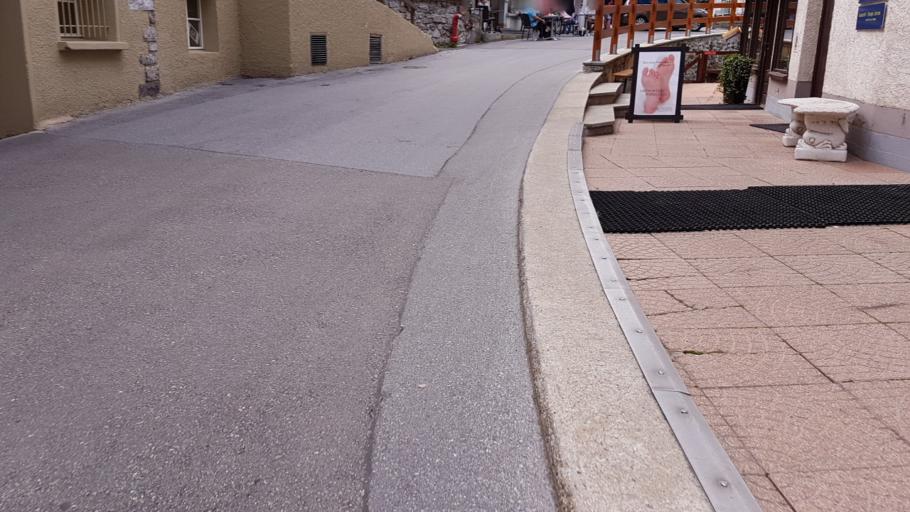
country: CH
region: Valais
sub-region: Leuk District
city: Leukerbad
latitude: 46.3802
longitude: 7.6293
